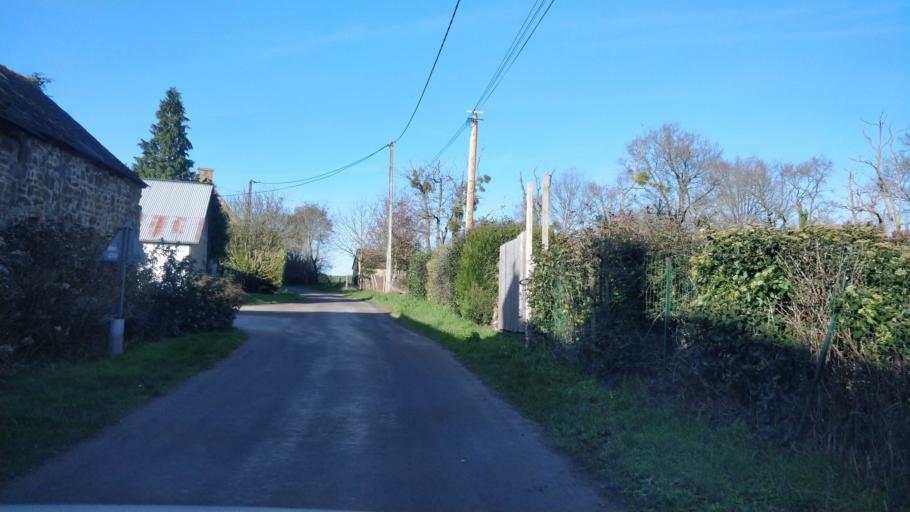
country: FR
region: Brittany
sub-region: Departement d'Ille-et-Vilaine
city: Sens-de-Bretagne
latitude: 48.3522
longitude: -1.4894
